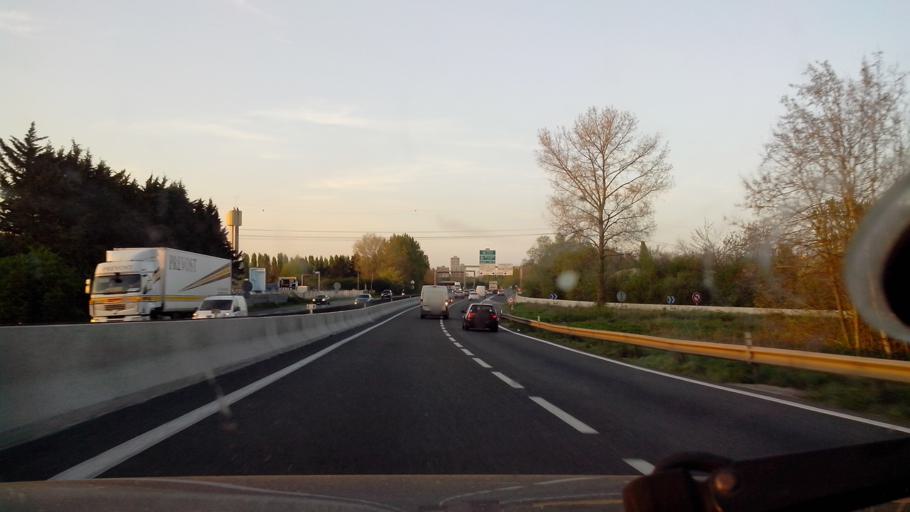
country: FR
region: Ile-de-France
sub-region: Departement de Seine-et-Marne
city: Pontault-Combault
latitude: 48.7751
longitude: 2.6124
